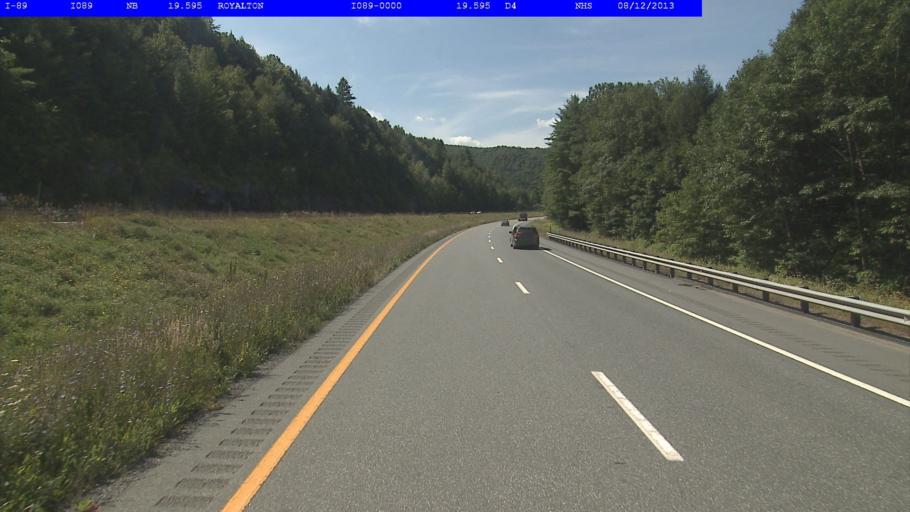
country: US
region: Vermont
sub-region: Orange County
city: Randolph
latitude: 43.8167
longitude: -72.5410
